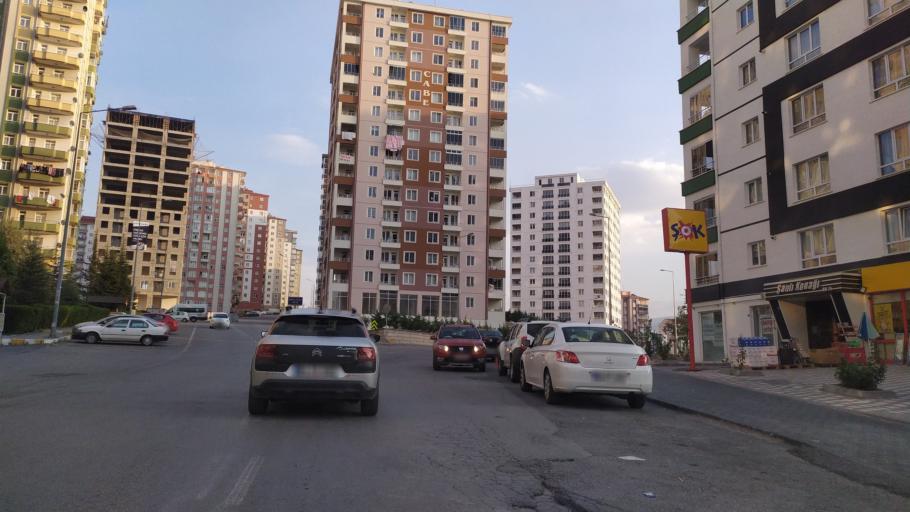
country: TR
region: Kayseri
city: Talas
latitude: 38.7034
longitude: 35.5617
